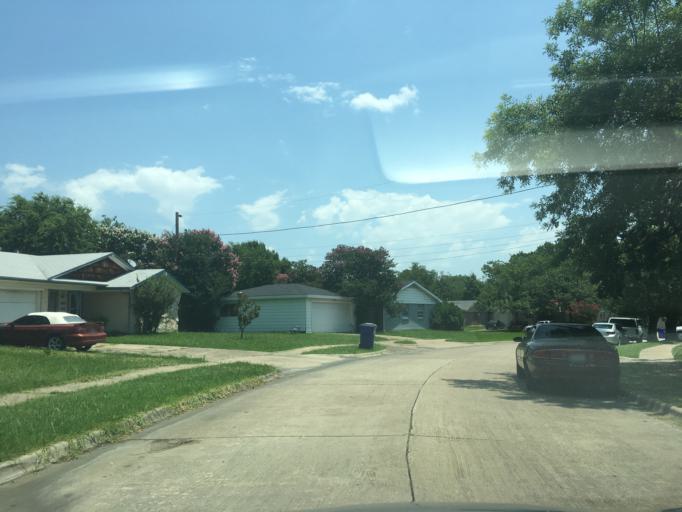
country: US
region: Texas
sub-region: Dallas County
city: Carrollton
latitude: 32.9439
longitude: -96.8765
